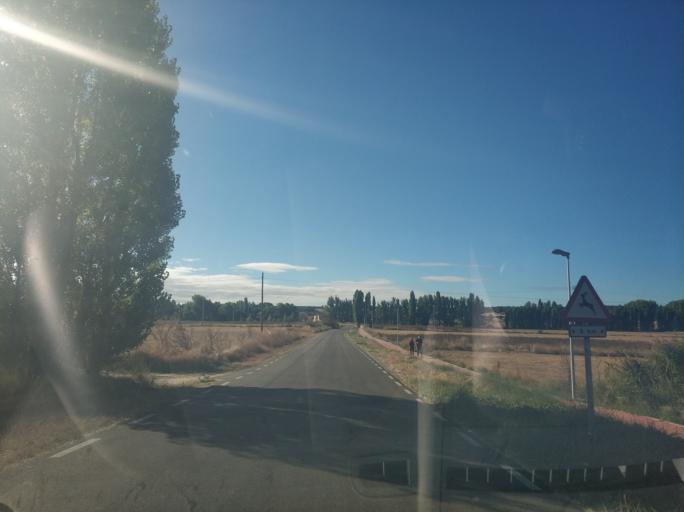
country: ES
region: Castille and Leon
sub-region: Provincia de Burgos
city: San Juan del Monte
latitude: 41.6905
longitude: -3.5215
